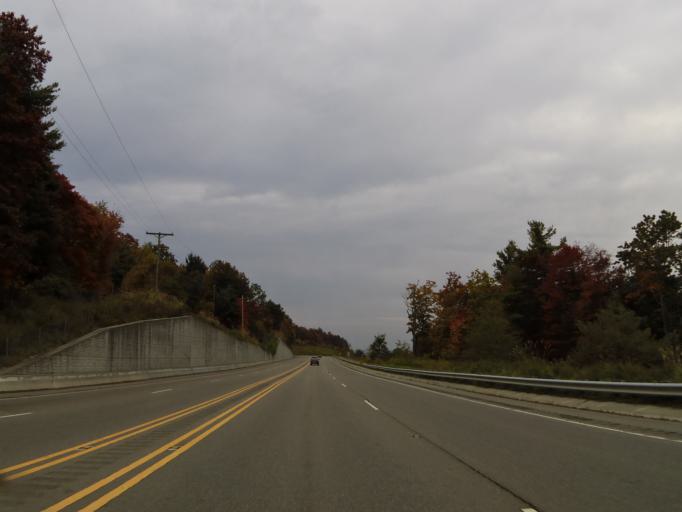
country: US
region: North Carolina
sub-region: Watauga County
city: Blowing Rock
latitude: 36.0927
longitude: -81.6372
